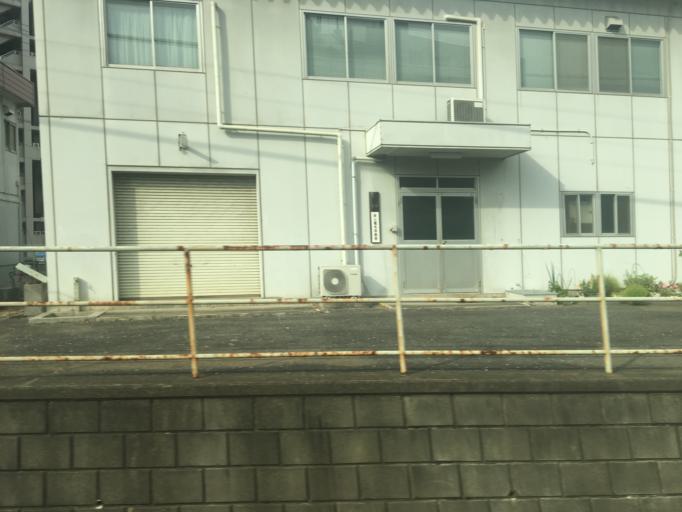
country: JP
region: Saitama
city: Sayama
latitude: 35.8562
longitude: 139.4131
